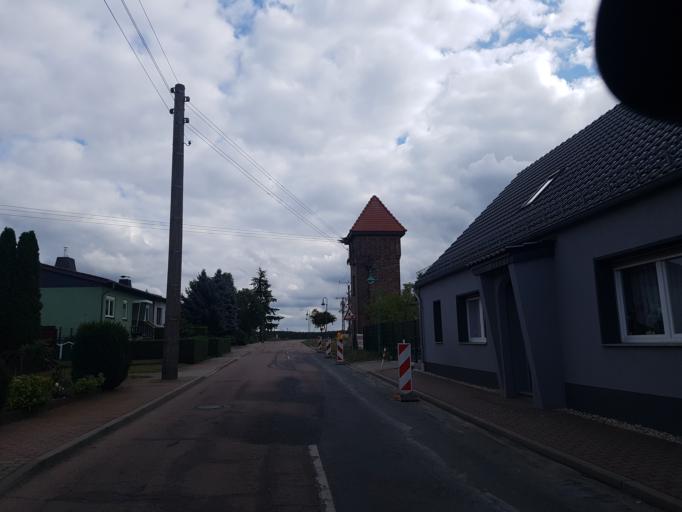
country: DE
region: Saxony-Anhalt
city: Rosslau
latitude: 51.9796
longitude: 12.2975
